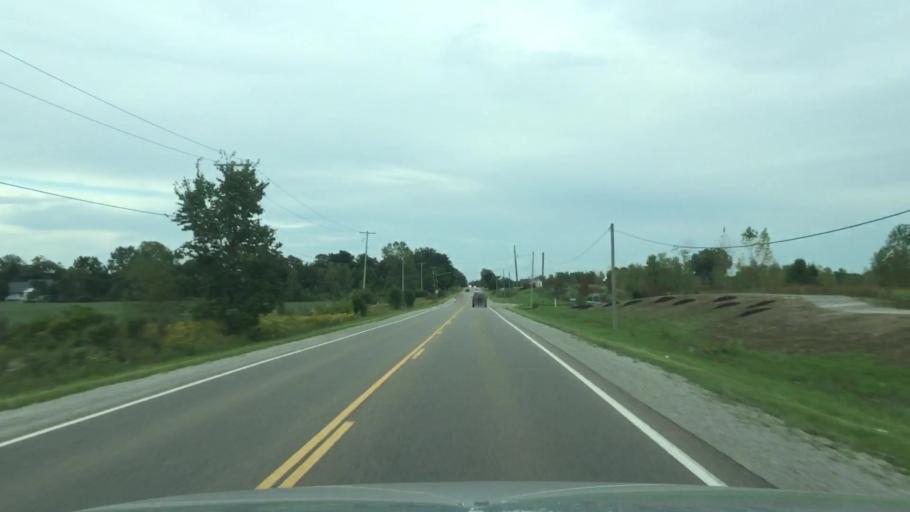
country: US
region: Michigan
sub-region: Genesee County
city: Lake Fenton
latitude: 42.8859
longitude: -83.6849
